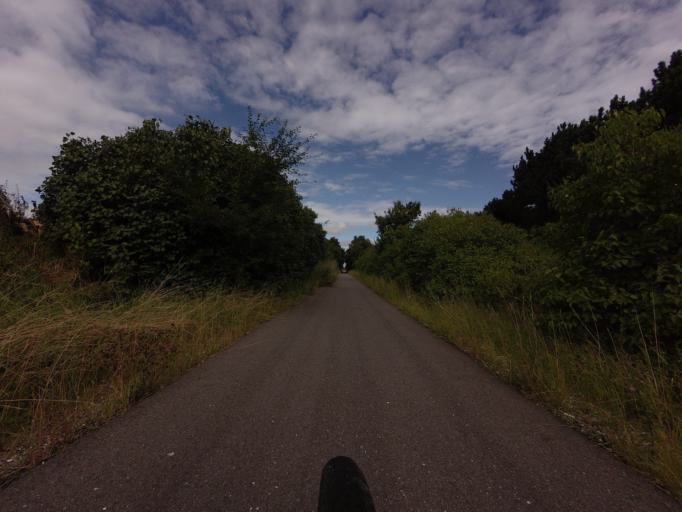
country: DK
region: Central Jutland
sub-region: Norddjurs Kommune
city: Auning
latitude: 56.4247
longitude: 10.3818
